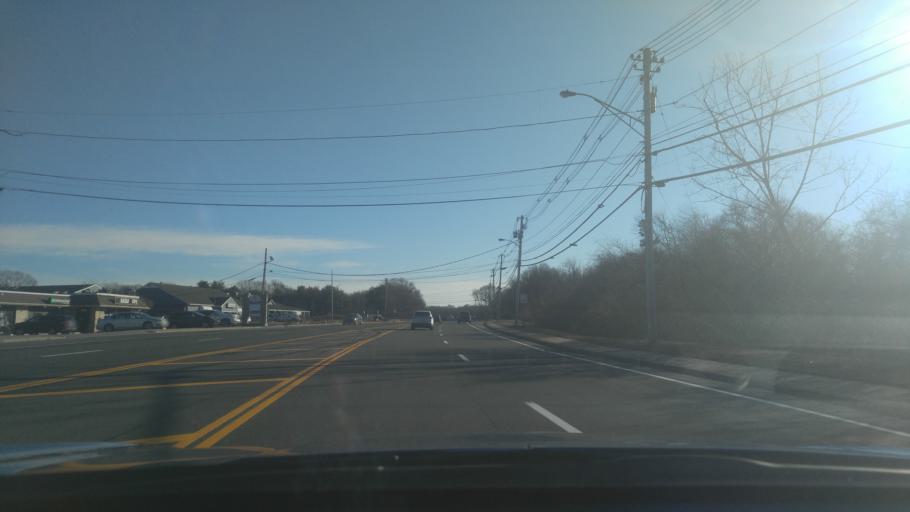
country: US
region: Rhode Island
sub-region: Washington County
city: Narragansett Pier
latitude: 41.4275
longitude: -71.4808
